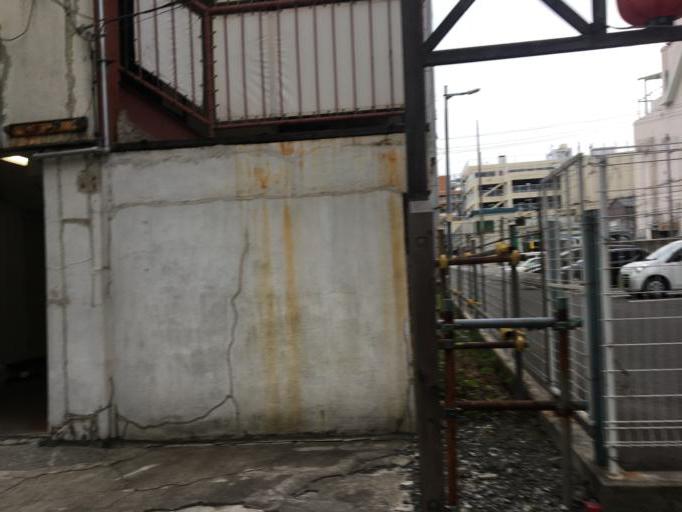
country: JP
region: Aomori
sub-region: Hachinohe Shi
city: Uchimaru
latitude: 40.5091
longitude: 141.4933
